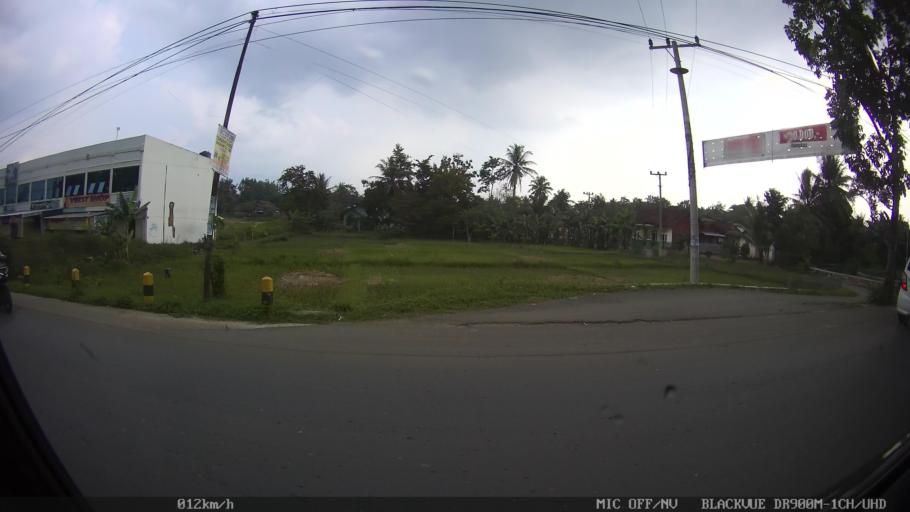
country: ID
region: Lampung
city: Gadingrejo
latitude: -5.3720
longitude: 105.0769
